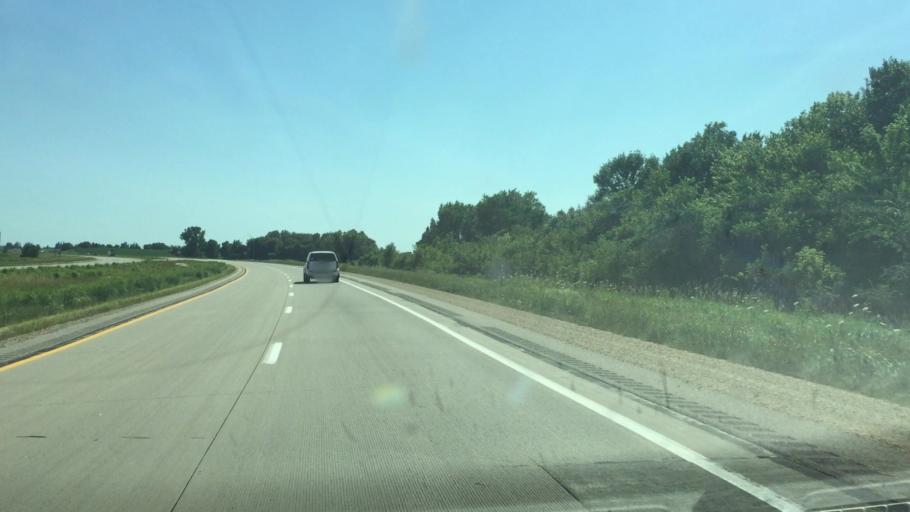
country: US
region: Iowa
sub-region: Jones County
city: Monticello
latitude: 42.1986
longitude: -91.2112
